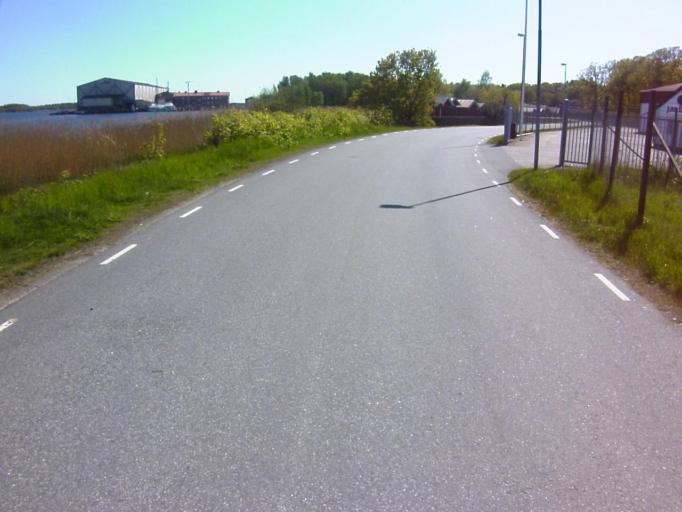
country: SE
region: Blekinge
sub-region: Solvesborgs Kommun
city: Soelvesborg
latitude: 56.0456
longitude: 14.5815
